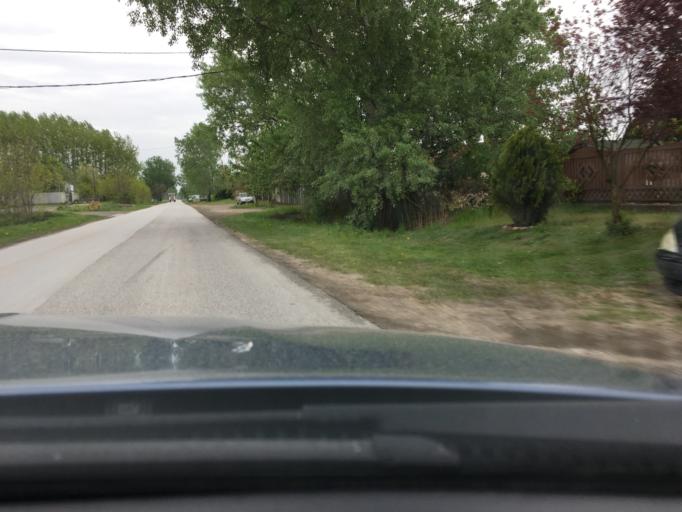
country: HU
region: Hajdu-Bihar
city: Debrecen
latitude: 47.5491
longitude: 21.6820
